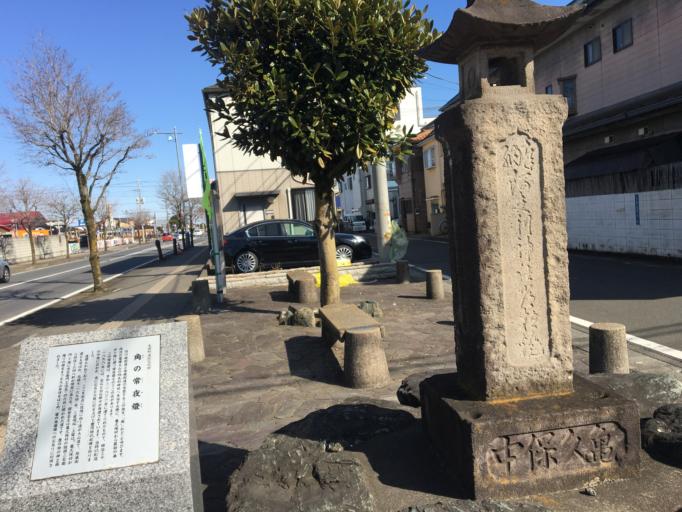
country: JP
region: Saitama
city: Kamifukuoka
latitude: 35.8599
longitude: 139.5109
